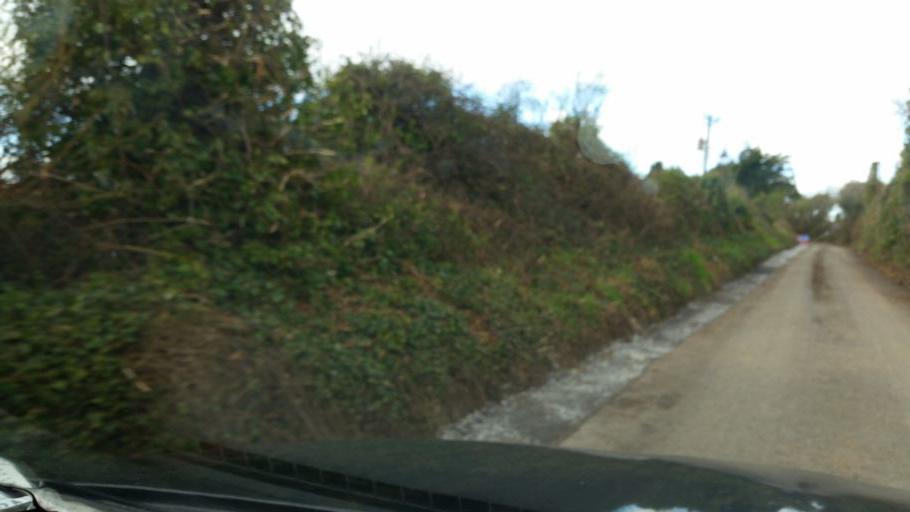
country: IE
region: Leinster
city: Kinsealy-Drinan
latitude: 53.4422
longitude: -6.2199
